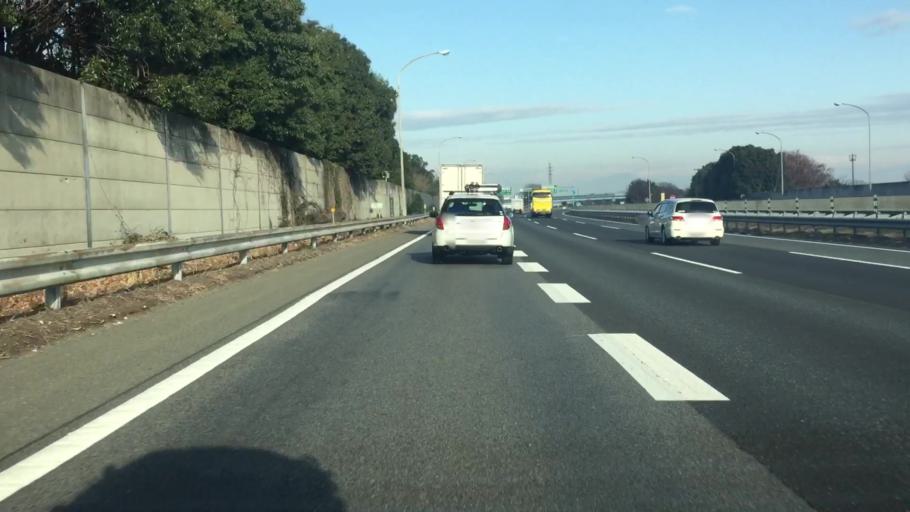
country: JP
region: Gunma
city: Fujioka
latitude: 36.2676
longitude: 139.0972
